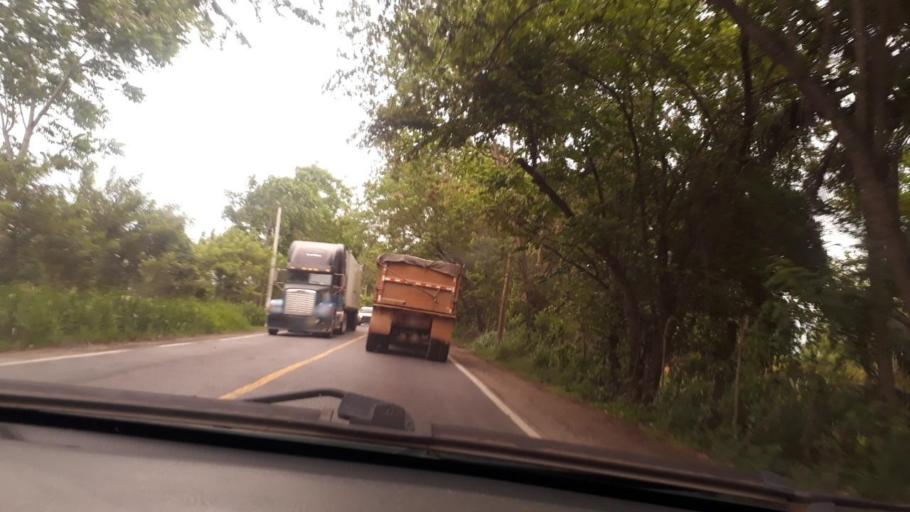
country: GT
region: Izabal
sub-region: Municipio de Los Amates
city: Los Amates
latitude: 15.3004
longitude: -89.0635
